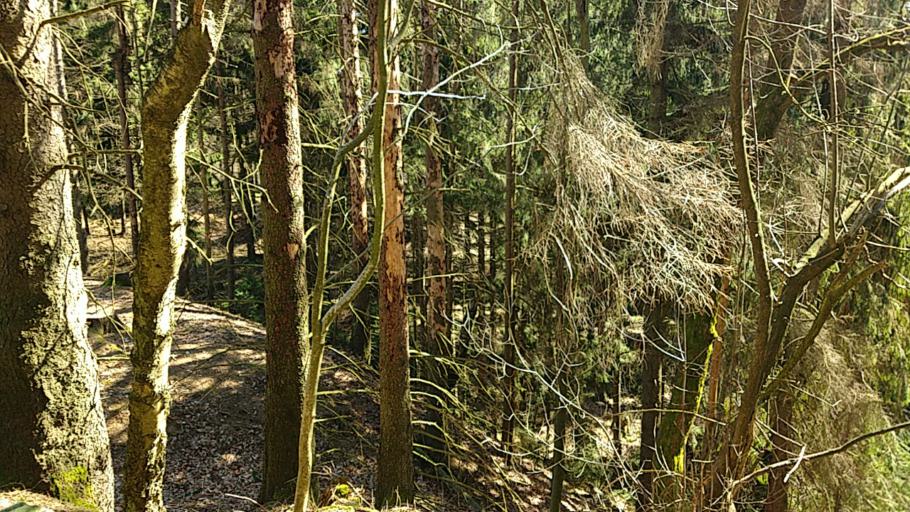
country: DE
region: Lower Saxony
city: Hameln
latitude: 52.1605
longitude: 9.3996
